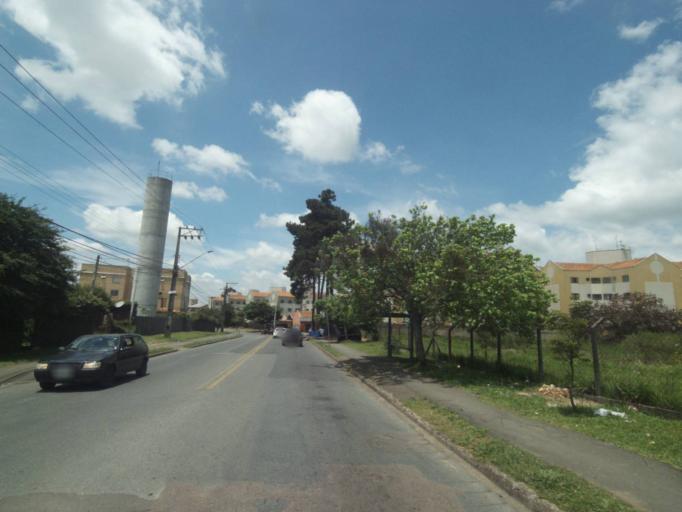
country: BR
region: Parana
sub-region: Curitiba
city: Curitiba
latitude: -25.4690
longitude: -49.3436
